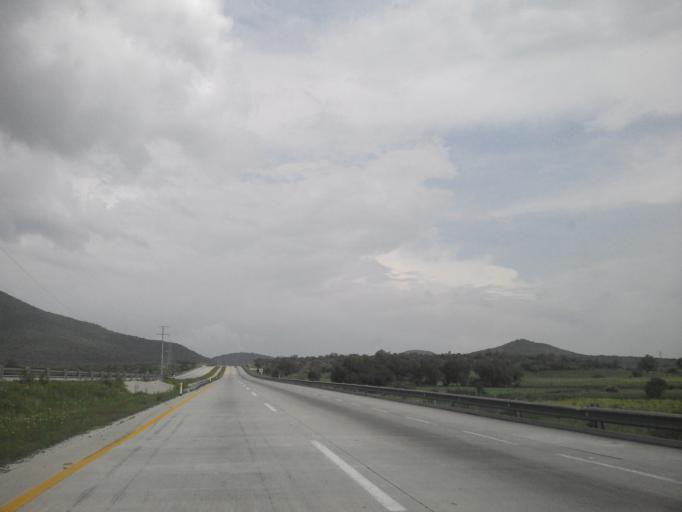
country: MX
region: Hidalgo
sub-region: Atitalaquia
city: Tezoquipa
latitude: 20.0407
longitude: -99.1814
